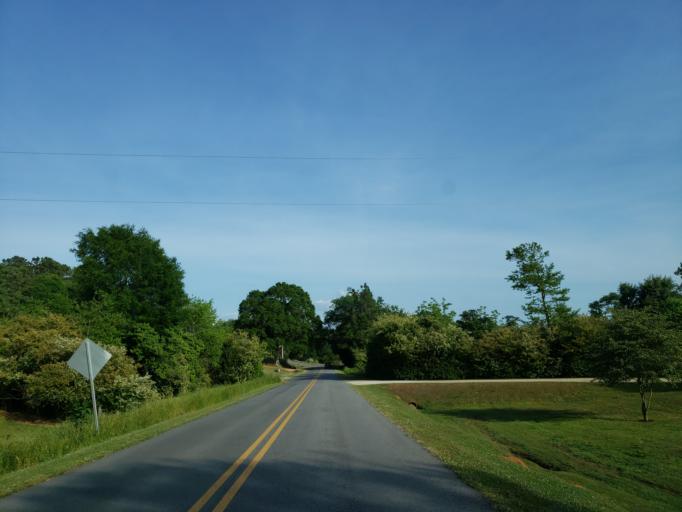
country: US
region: Georgia
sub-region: Carroll County
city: Bowdon
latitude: 33.5036
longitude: -85.3287
